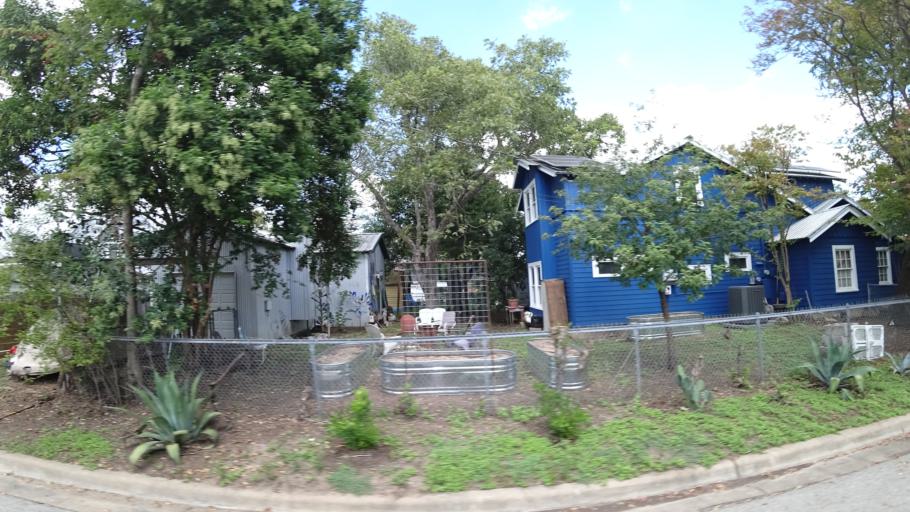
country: US
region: Texas
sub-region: Travis County
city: Austin
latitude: 30.3181
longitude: -97.7190
